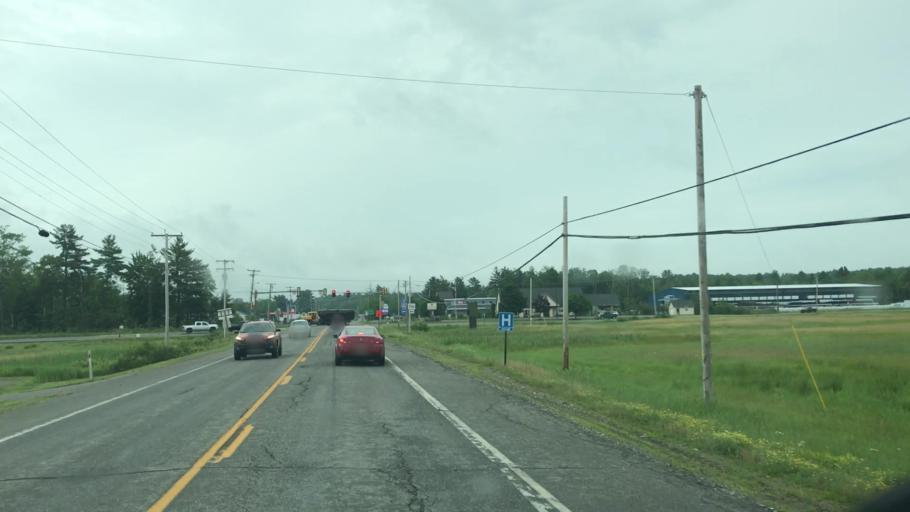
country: US
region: Maine
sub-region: Penobscot County
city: Lincoln
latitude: 45.3528
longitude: -68.5339
